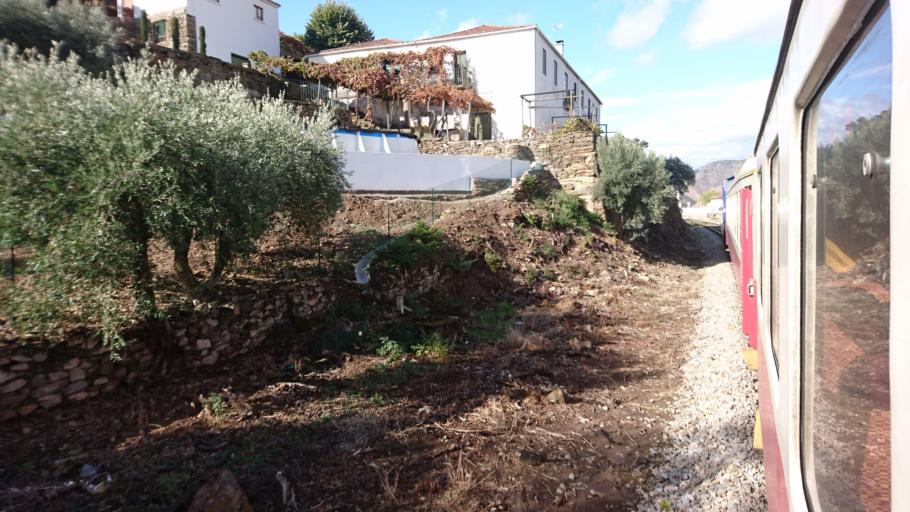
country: PT
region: Guarda
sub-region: Vila Nova de Foz Coa
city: Vila Nova de Foz Coa
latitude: 41.1343
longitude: -7.2089
